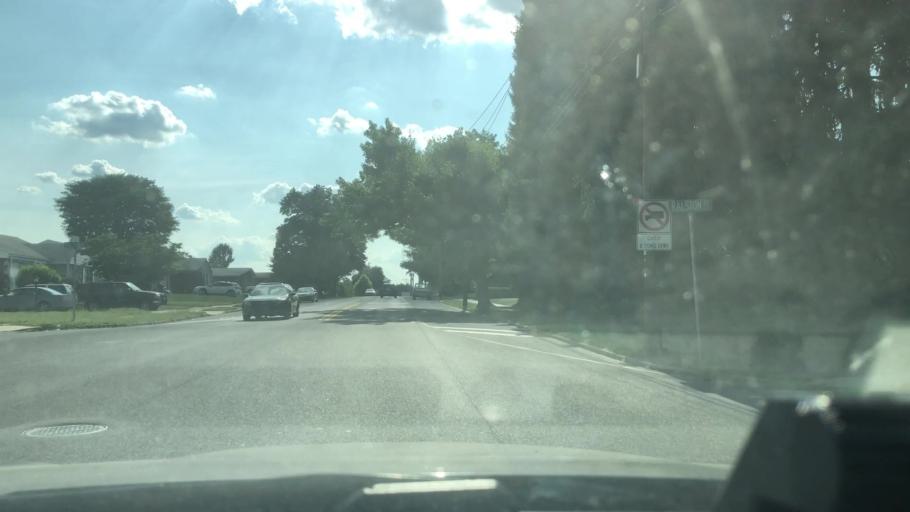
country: US
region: Pennsylvania
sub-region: Northampton County
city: Bethlehem
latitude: 40.6336
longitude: -75.3979
